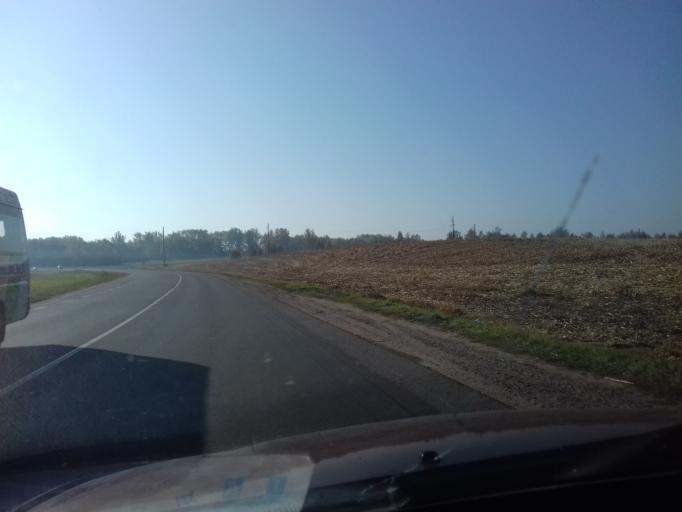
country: BY
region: Minsk
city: Hatava
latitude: 53.7715
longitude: 27.6372
